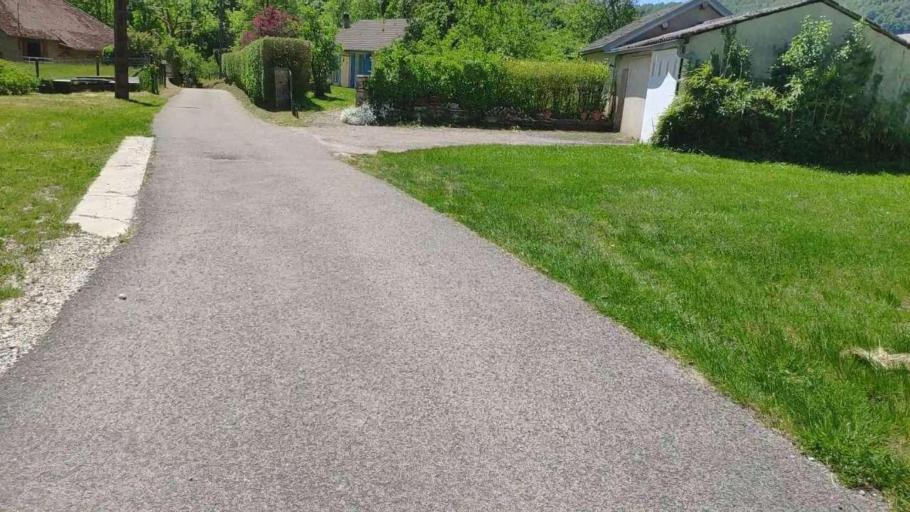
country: FR
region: Franche-Comte
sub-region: Departement du Jura
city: Poligny
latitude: 46.7615
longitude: 5.6830
